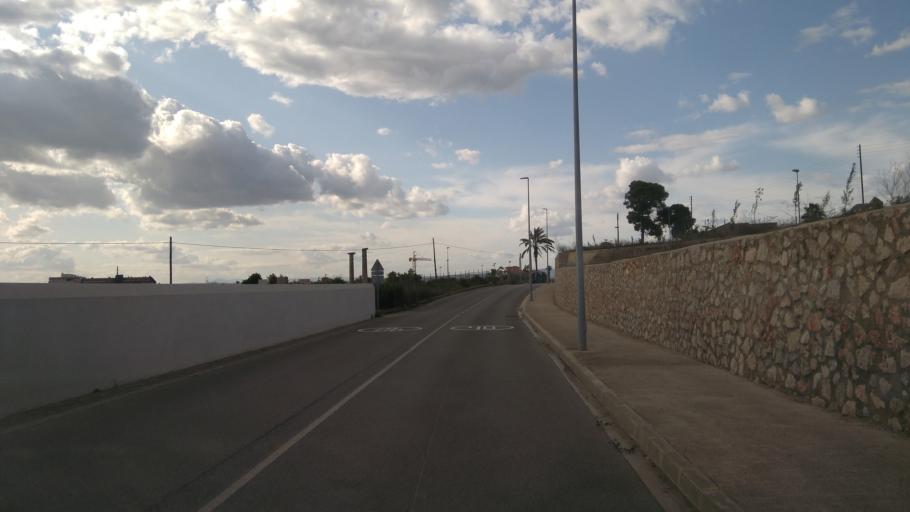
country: ES
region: Valencia
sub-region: Provincia de Valencia
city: Alzira
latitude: 39.1502
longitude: -0.4189
